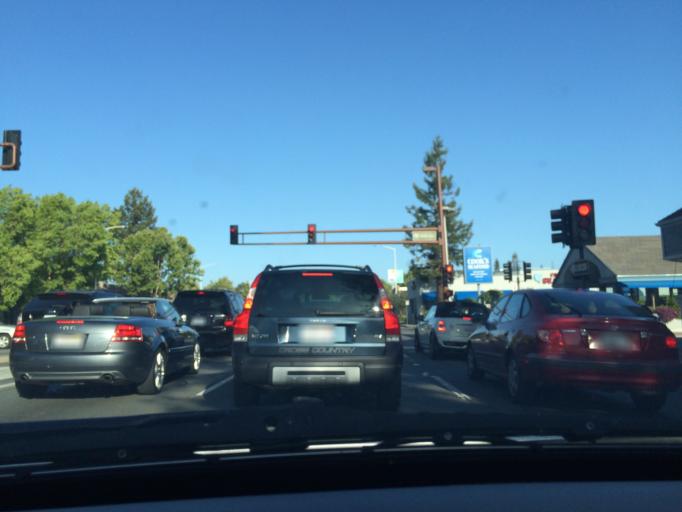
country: US
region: California
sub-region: San Mateo County
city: Menlo Park
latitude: 37.4520
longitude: -122.1800
